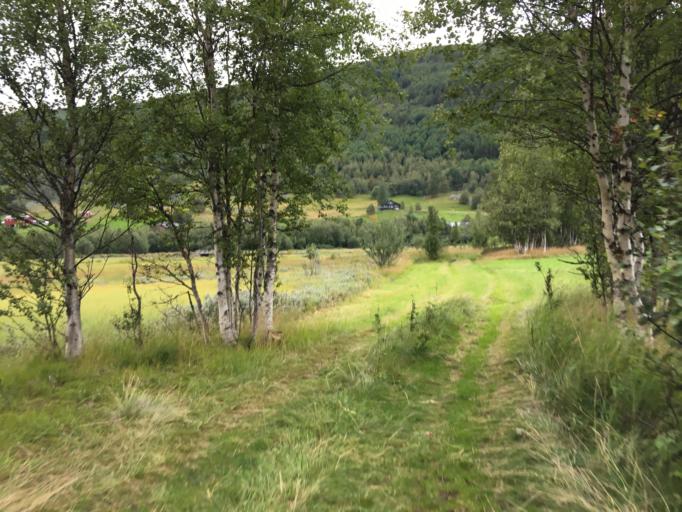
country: NO
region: Buskerud
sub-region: Hol
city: Hol
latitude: 60.6163
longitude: 8.2251
